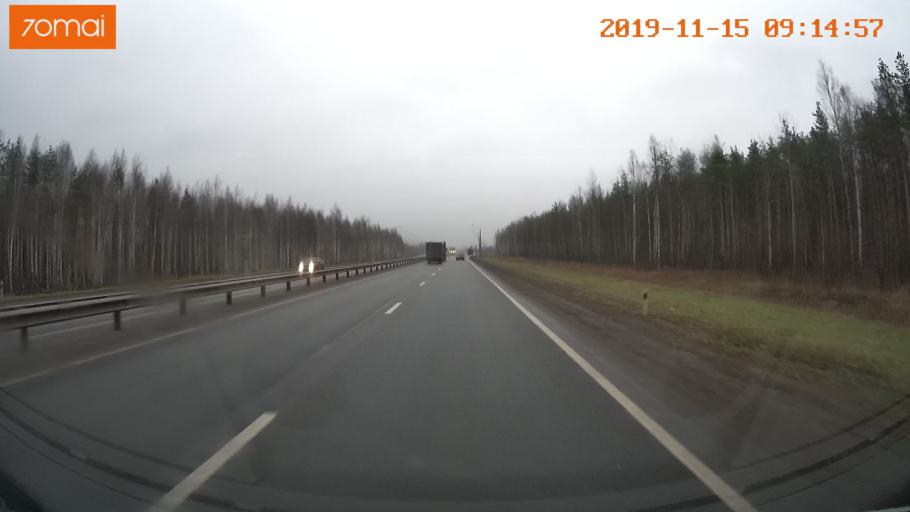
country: RU
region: Vologda
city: Tonshalovo
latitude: 59.2329
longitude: 37.9632
